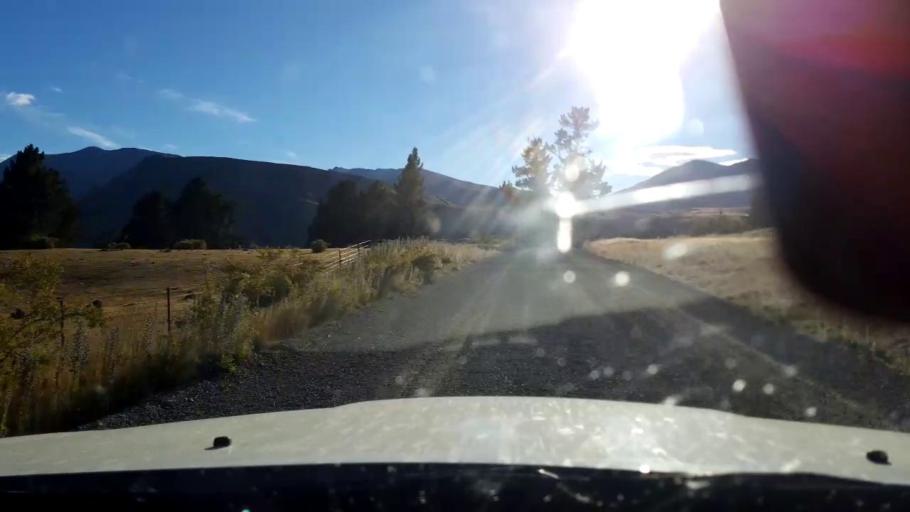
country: NZ
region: Canterbury
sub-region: Timaru District
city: Pleasant Point
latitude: -43.9642
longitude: 170.5269
